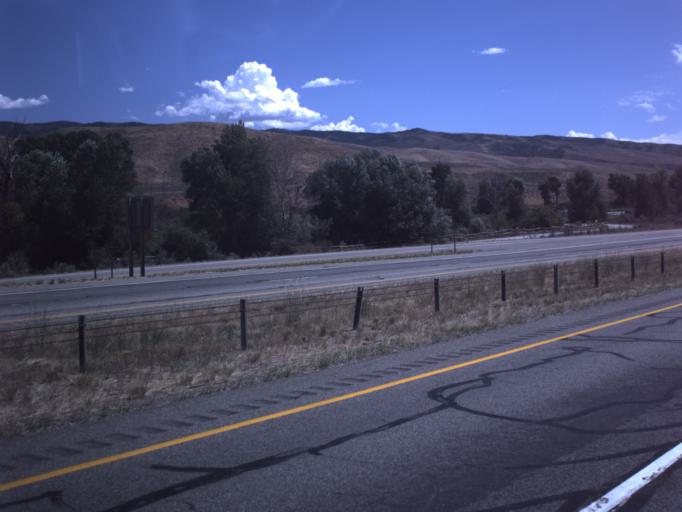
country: US
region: Utah
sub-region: Morgan County
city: Morgan
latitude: 41.0430
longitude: -111.5218
